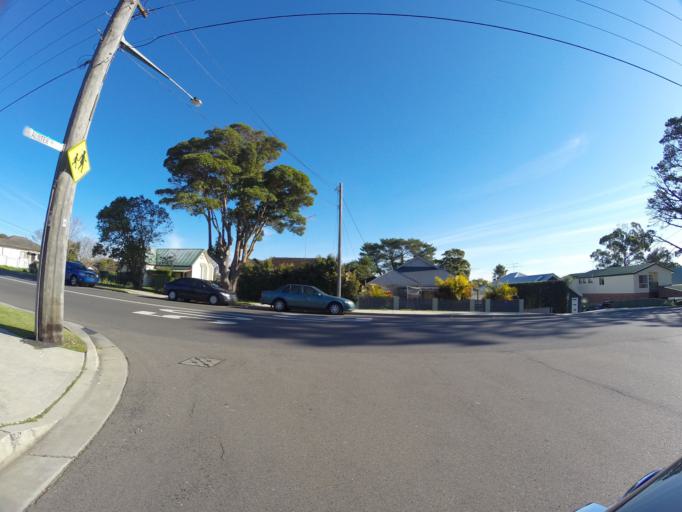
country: AU
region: New South Wales
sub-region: Sutherland Shire
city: Engadine
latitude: -34.0684
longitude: 151.0065
